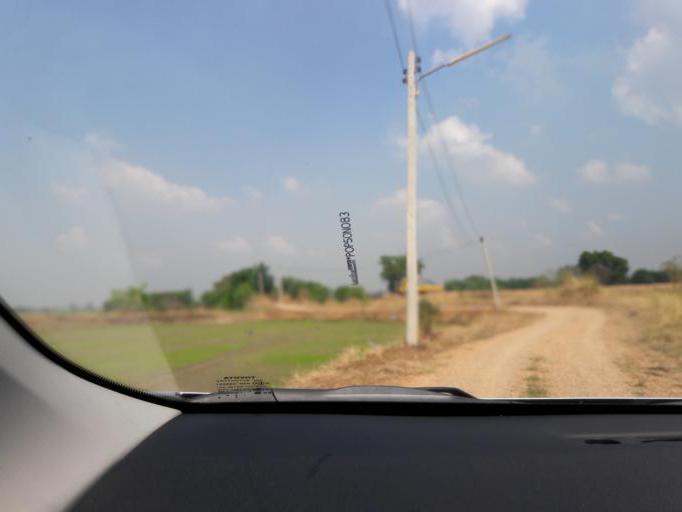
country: TH
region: Ang Thong
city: Ang Thong
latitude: 14.5632
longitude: 100.4103
